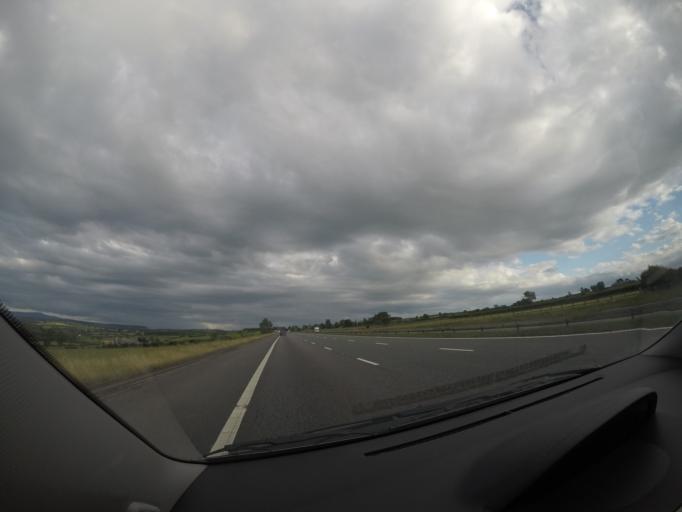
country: GB
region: England
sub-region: Cumbria
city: Scotby
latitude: 54.7807
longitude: -2.8550
